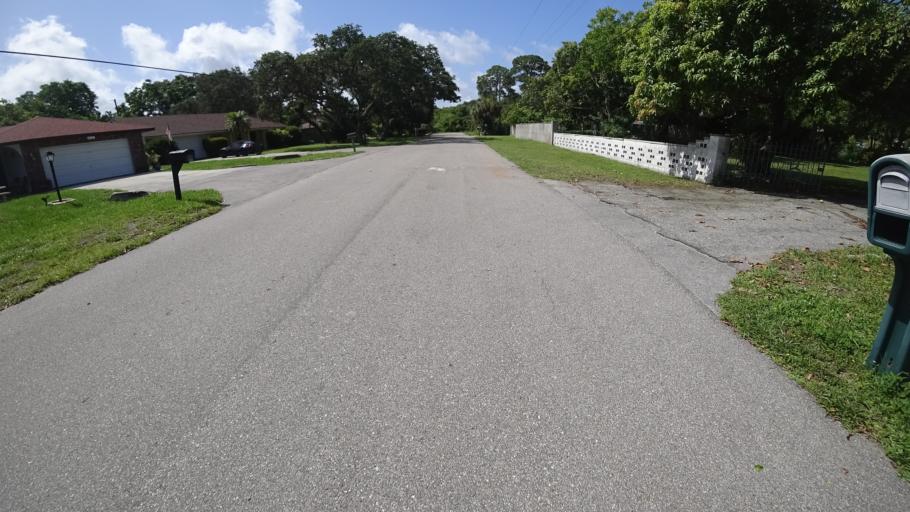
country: US
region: Florida
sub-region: Manatee County
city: Whitfield
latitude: 27.3942
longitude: -82.5670
